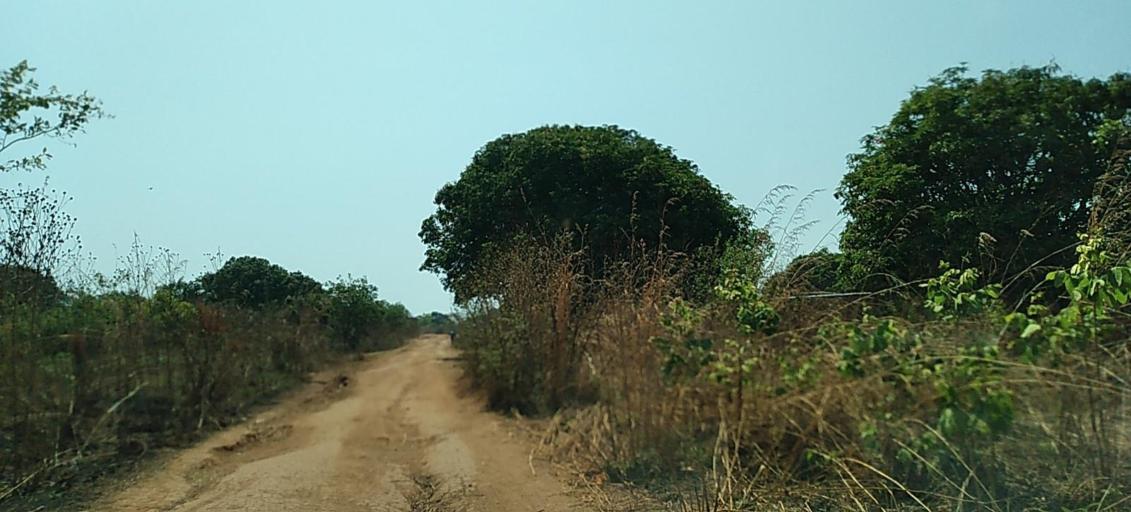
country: ZM
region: Copperbelt
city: Luanshya
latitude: -13.3484
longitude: 28.3975
